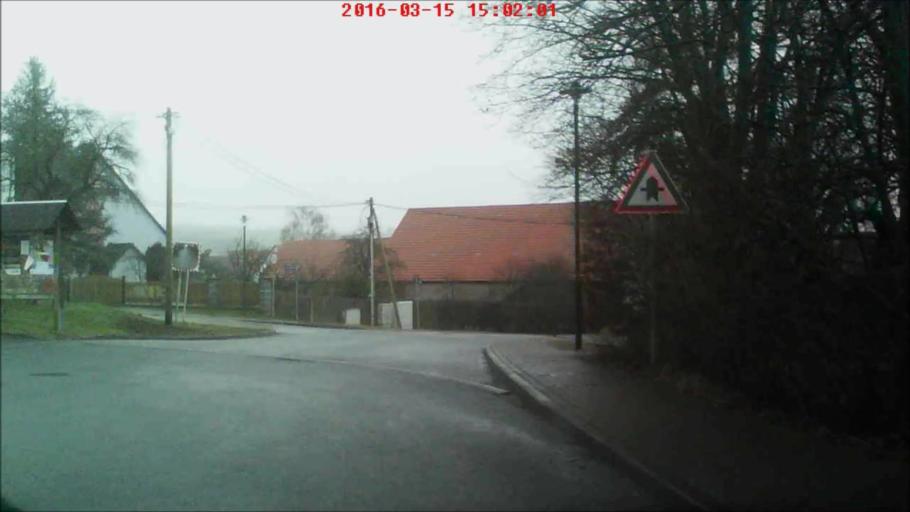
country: DE
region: Thuringia
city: Rockhausen
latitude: 50.9071
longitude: 11.0628
